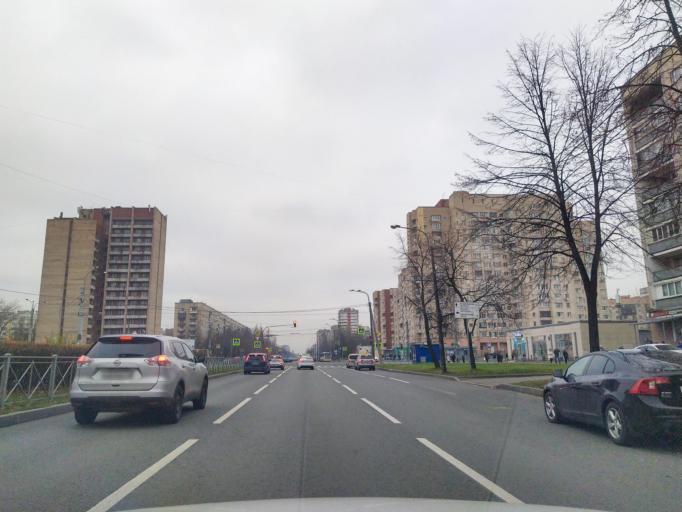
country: RU
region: St.-Petersburg
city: Sosnovka
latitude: 60.0389
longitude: 30.3458
